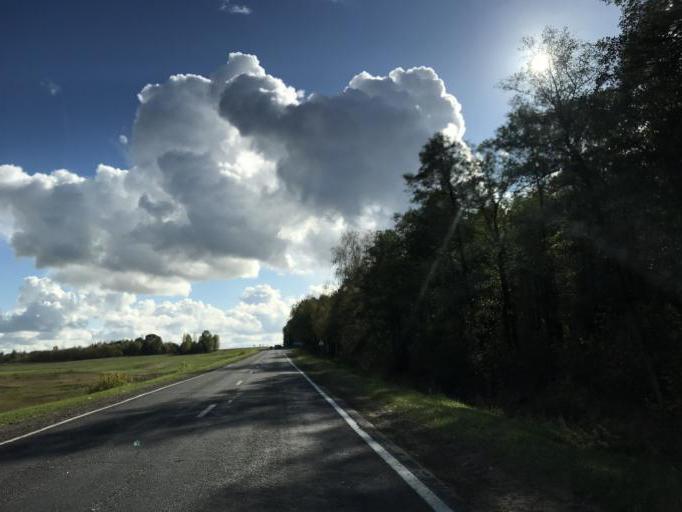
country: BY
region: Gomel
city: Buda-Kashalyova
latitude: 52.8722
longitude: 30.6817
